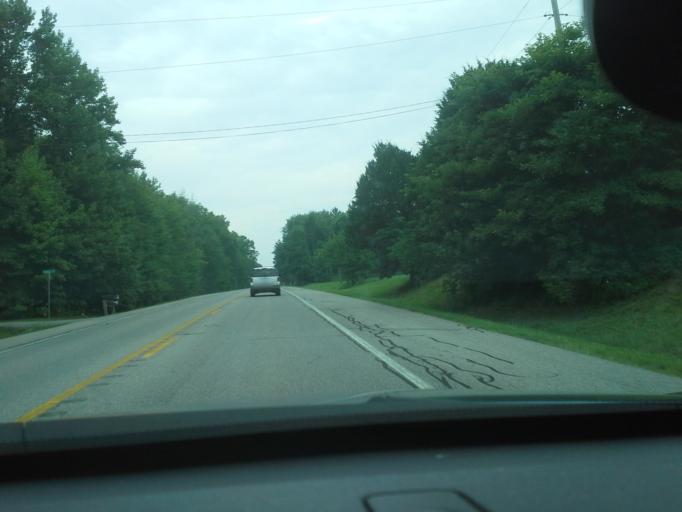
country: US
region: Maryland
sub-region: Calvert County
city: Owings
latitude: 38.7246
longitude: -76.6100
